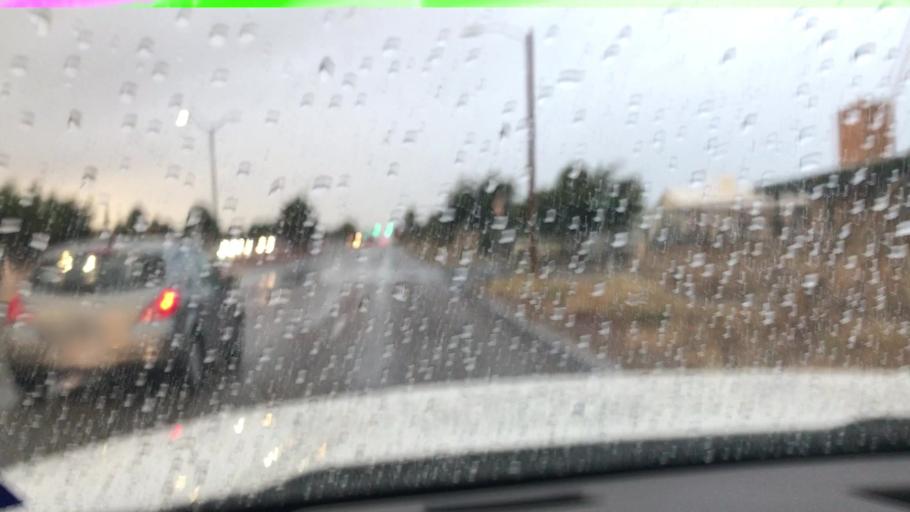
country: US
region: Texas
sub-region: El Paso County
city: Fort Bliss
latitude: 31.7955
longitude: -106.3234
